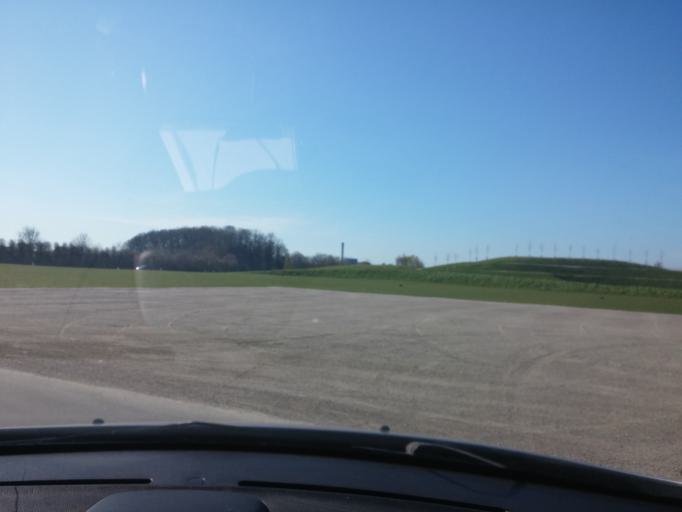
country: DK
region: Central Jutland
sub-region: Odder Kommune
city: Odder
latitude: 55.9211
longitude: 10.2491
